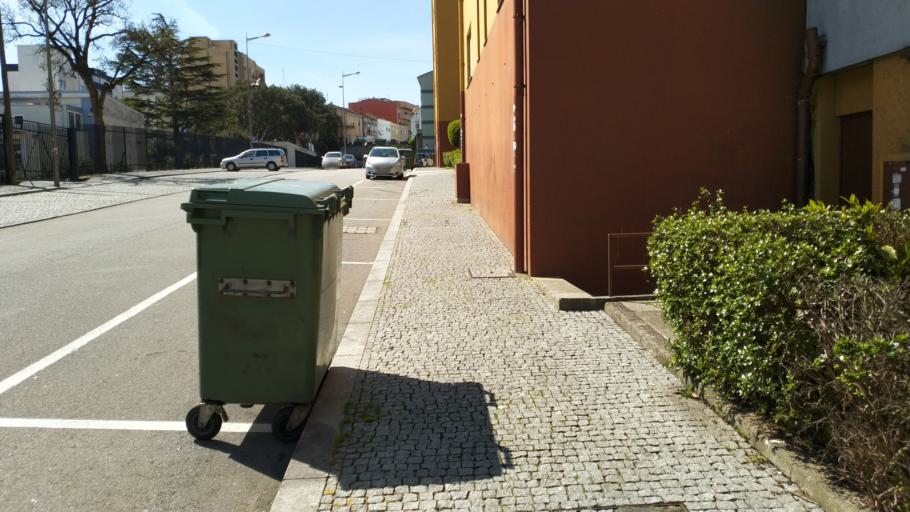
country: PT
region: Porto
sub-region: Vila Nova de Gaia
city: Vilar de Andorinho
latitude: 41.1238
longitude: -8.6027
